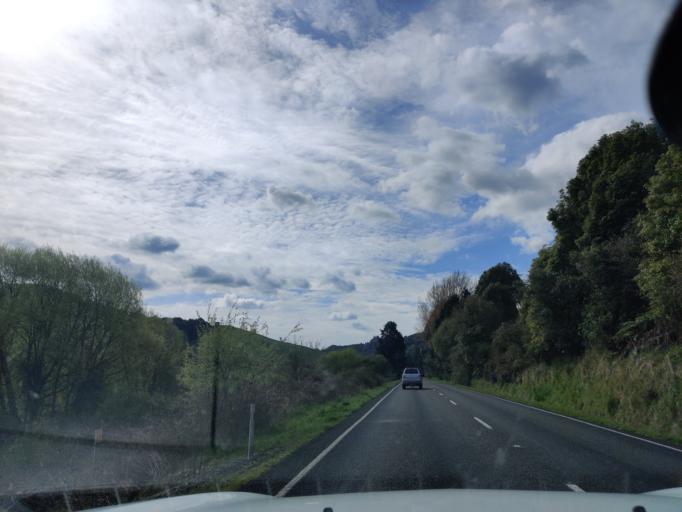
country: NZ
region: Waikato
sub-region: Otorohanga District
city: Otorohanga
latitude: -38.5595
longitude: 175.1962
